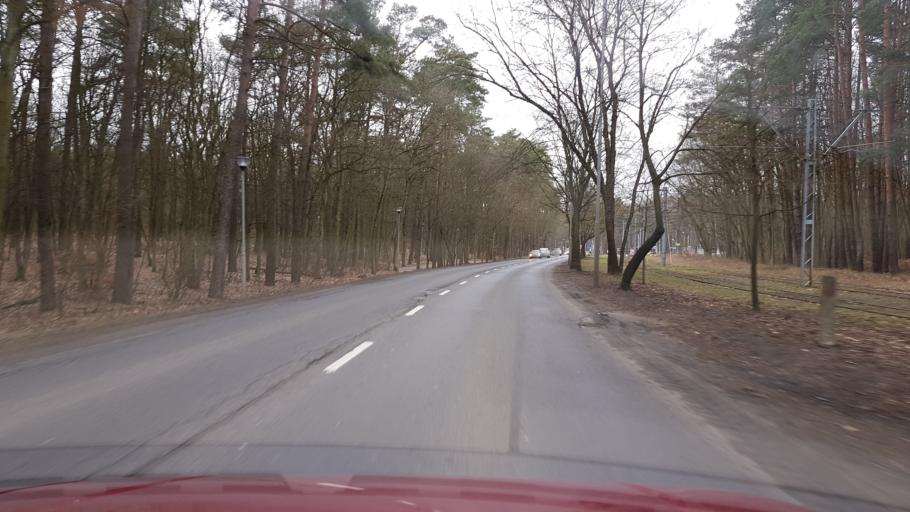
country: PL
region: West Pomeranian Voivodeship
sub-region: Szczecin
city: Szczecin
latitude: 53.4690
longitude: 14.4877
